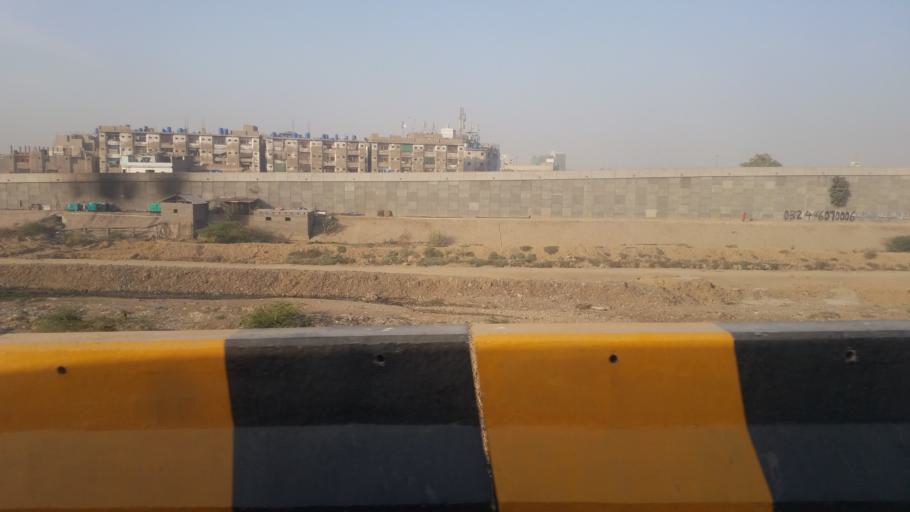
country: PK
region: Sindh
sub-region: Karachi District
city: Karachi
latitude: 24.9441
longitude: 67.0889
